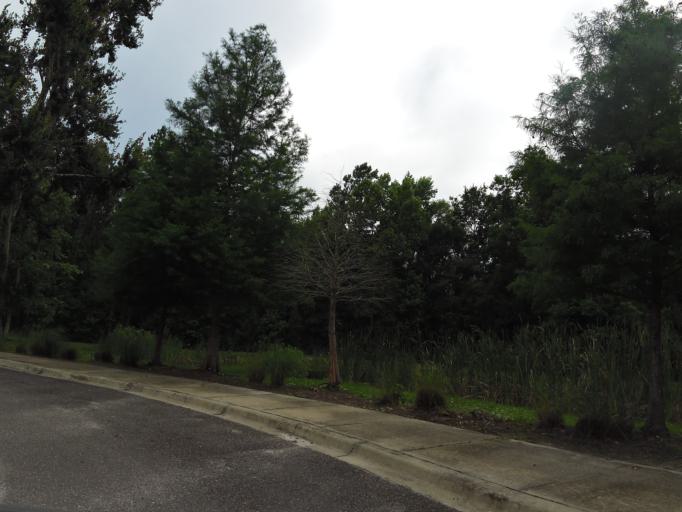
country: US
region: Florida
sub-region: Nassau County
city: Nassau Village-Ratliff
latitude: 30.5513
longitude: -81.7336
